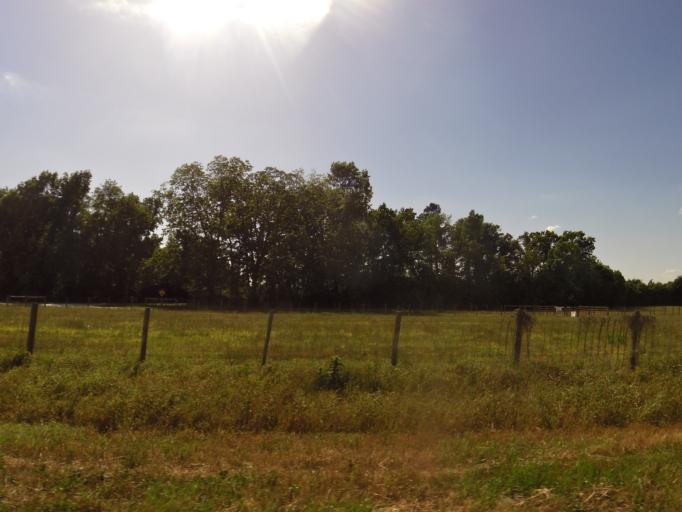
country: US
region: South Carolina
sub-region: Allendale County
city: Fairfax
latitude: 33.0683
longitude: -81.2130
